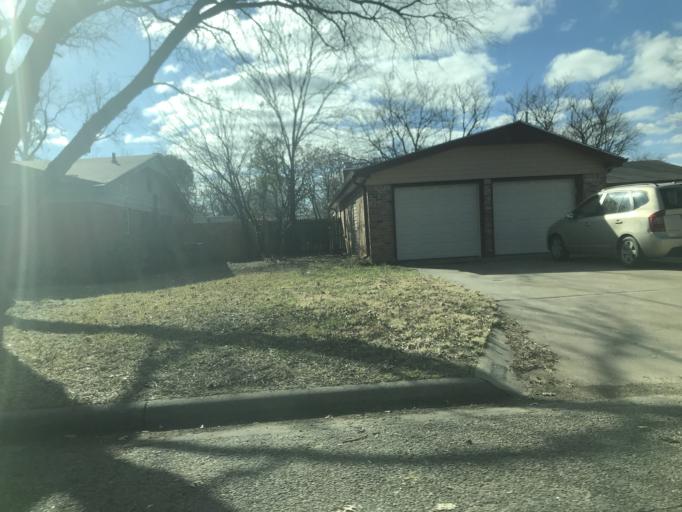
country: US
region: Texas
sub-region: Taylor County
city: Abilene
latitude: 32.4637
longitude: -99.7706
